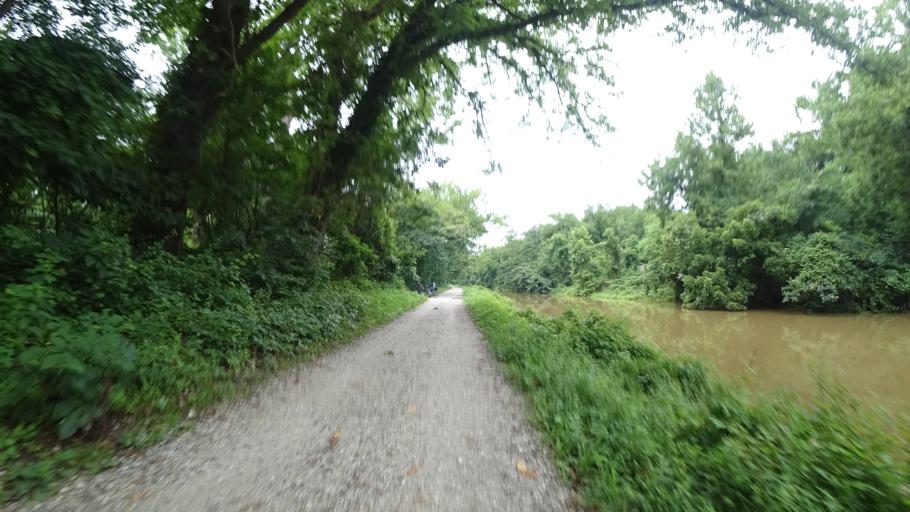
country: US
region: Maryland
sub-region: Montgomery County
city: Brookmont
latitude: 38.9366
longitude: -77.1176
